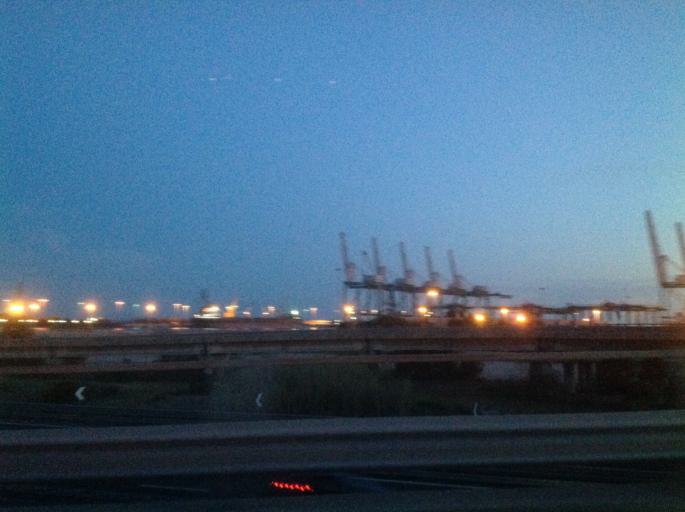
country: IT
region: Apulia
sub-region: Provincia di Taranto
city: Statte
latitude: 40.5098
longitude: 17.1605
